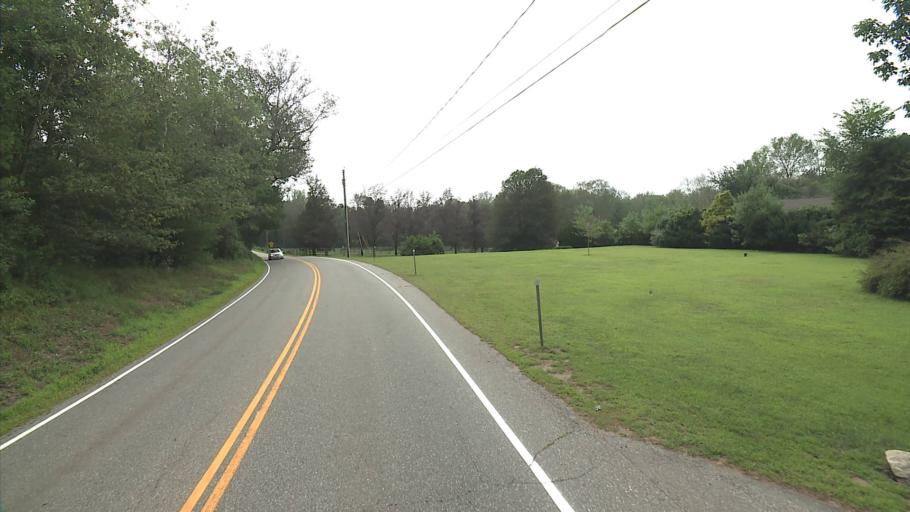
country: US
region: Connecticut
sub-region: Windham County
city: Wauregan
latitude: 41.7680
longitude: -71.9386
